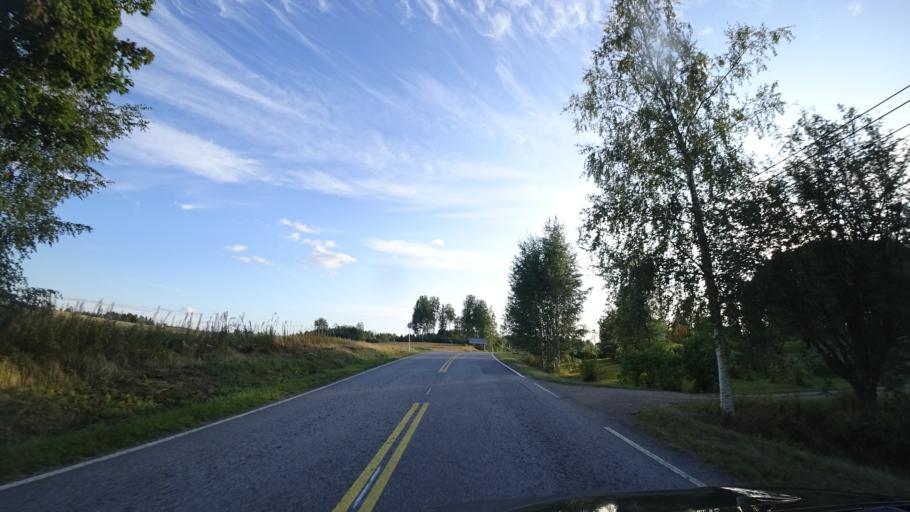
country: FI
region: Haeme
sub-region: Haemeenlinna
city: Lammi
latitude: 61.0357
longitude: 24.9245
